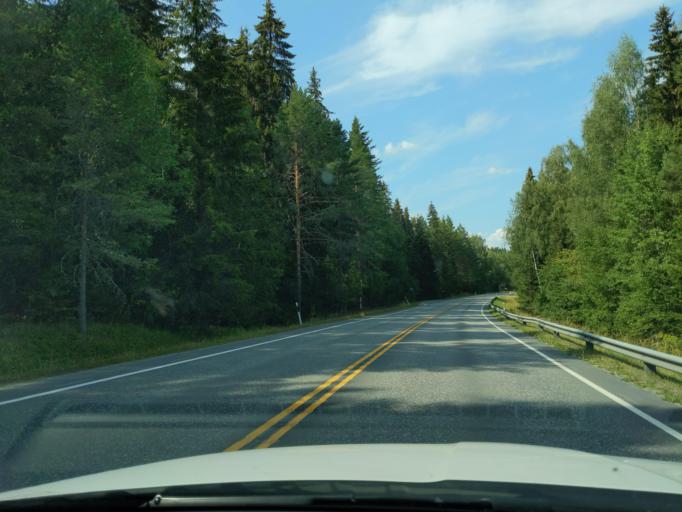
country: FI
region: Paijanne Tavastia
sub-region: Lahti
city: Padasjoki
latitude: 61.3796
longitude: 25.1948
